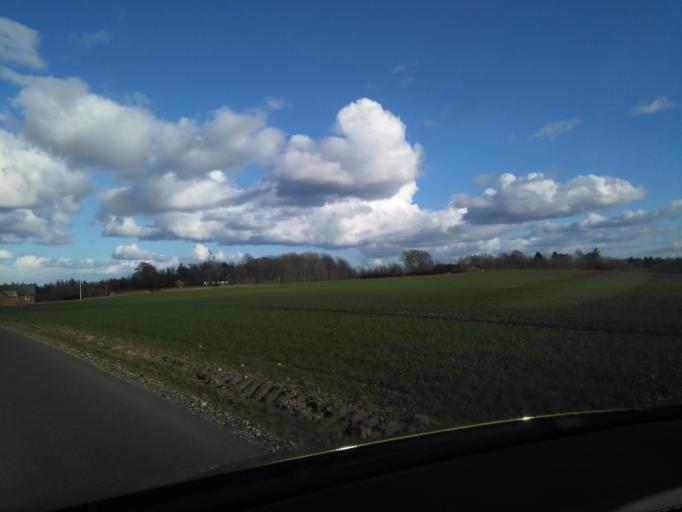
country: DK
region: Central Jutland
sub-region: Silkeborg Kommune
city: Silkeborg
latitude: 56.1916
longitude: 9.4706
